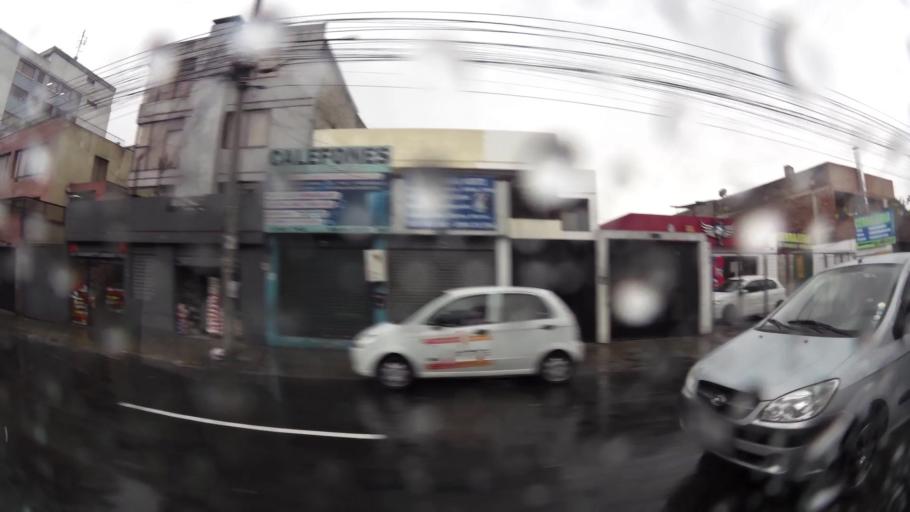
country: EC
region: Pichincha
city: Quito
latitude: -0.1584
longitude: -78.4666
